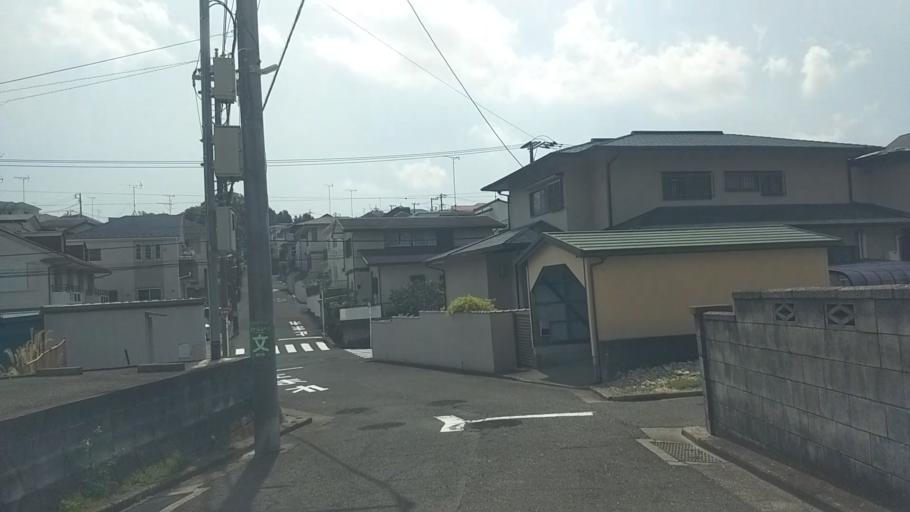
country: JP
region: Kanagawa
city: Yokohama
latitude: 35.3907
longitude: 139.5919
